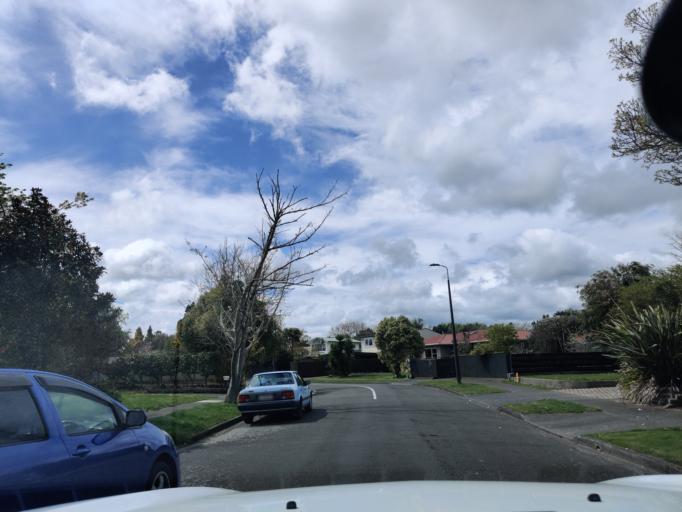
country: NZ
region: Manawatu-Wanganui
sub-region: Palmerston North City
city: Palmerston North
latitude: -40.3797
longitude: 175.5969
